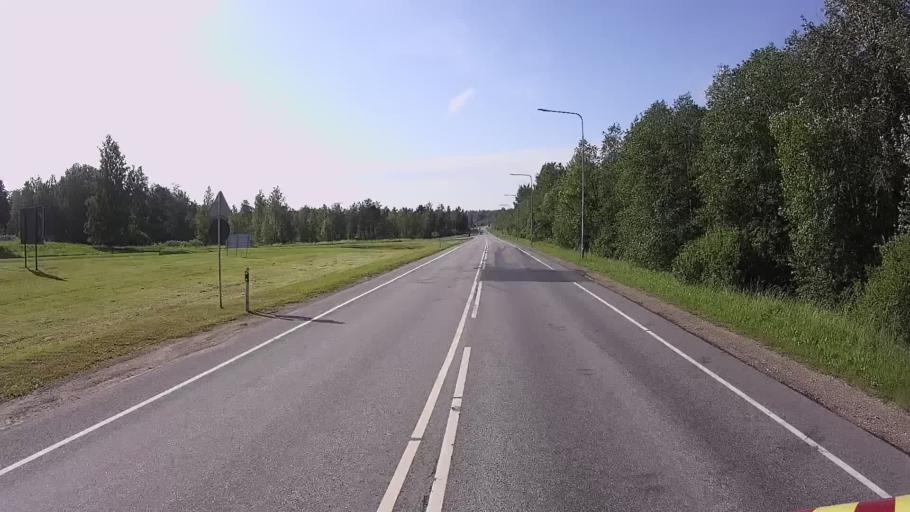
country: EE
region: Viljandimaa
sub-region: Viljandi linn
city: Viljandi
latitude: 58.3382
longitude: 25.5698
